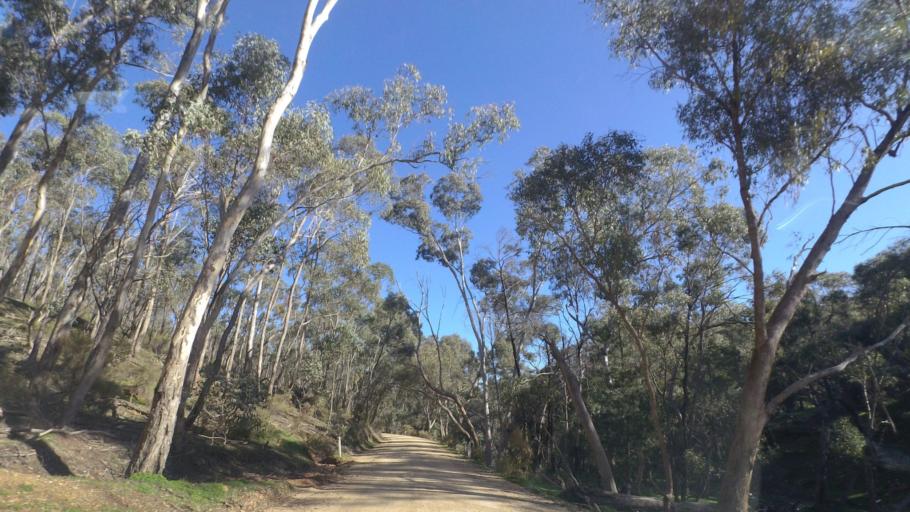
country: AU
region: Victoria
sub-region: Mount Alexander
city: Castlemaine
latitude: -37.0317
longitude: 144.2663
